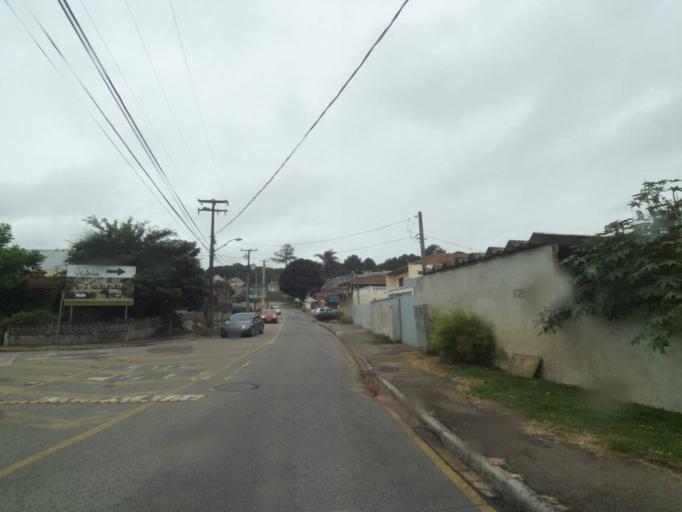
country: BR
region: Parana
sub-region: Curitiba
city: Curitiba
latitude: -25.4290
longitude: -49.3376
